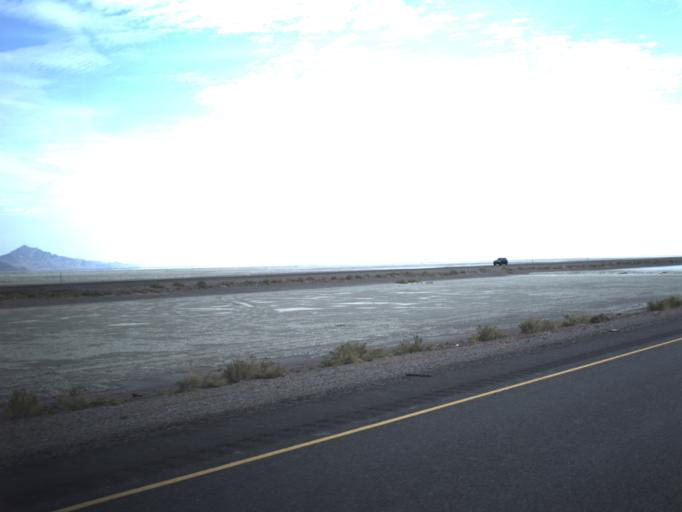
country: US
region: Utah
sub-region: Tooele County
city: Wendover
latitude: 40.7405
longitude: -113.9493
